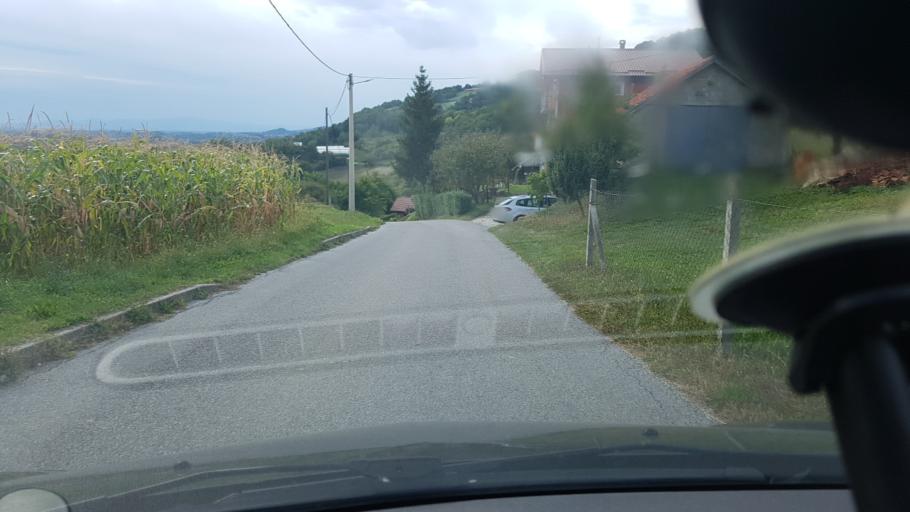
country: HR
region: Krapinsko-Zagorska
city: Radoboj
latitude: 46.1716
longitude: 15.9400
